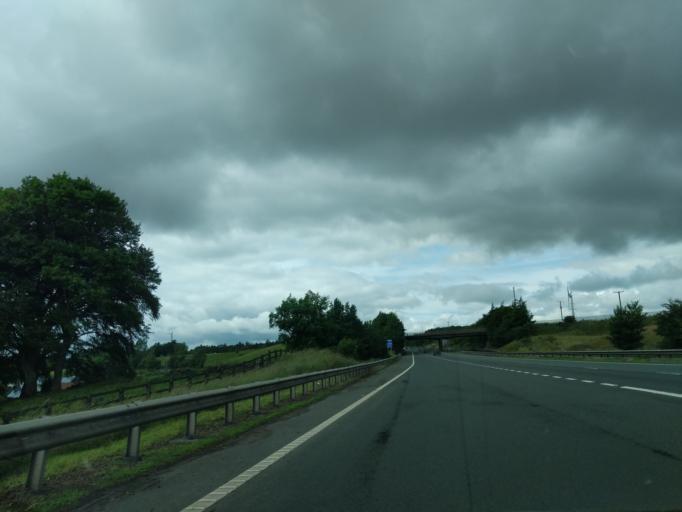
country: GB
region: Scotland
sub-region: South Lanarkshire
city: Douglas
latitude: 55.5966
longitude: -3.8343
